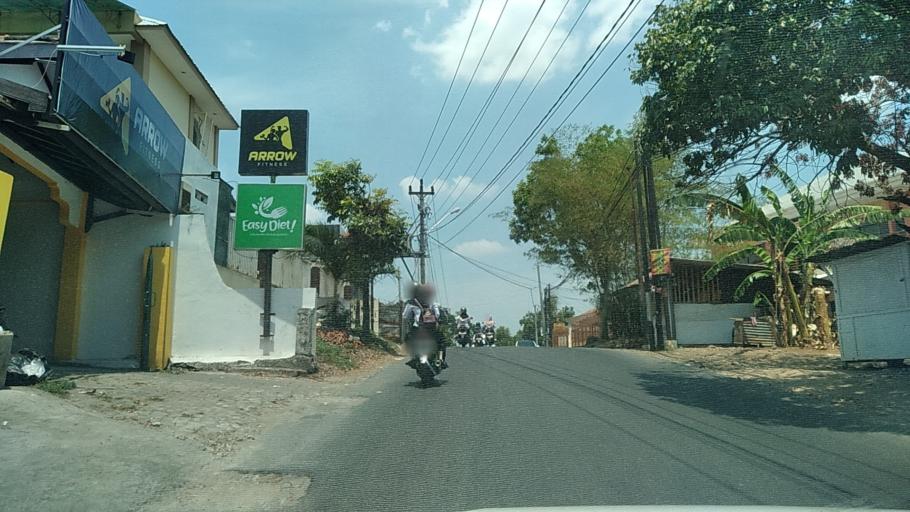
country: ID
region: Central Java
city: Semarang
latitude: -7.0290
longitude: 110.4075
